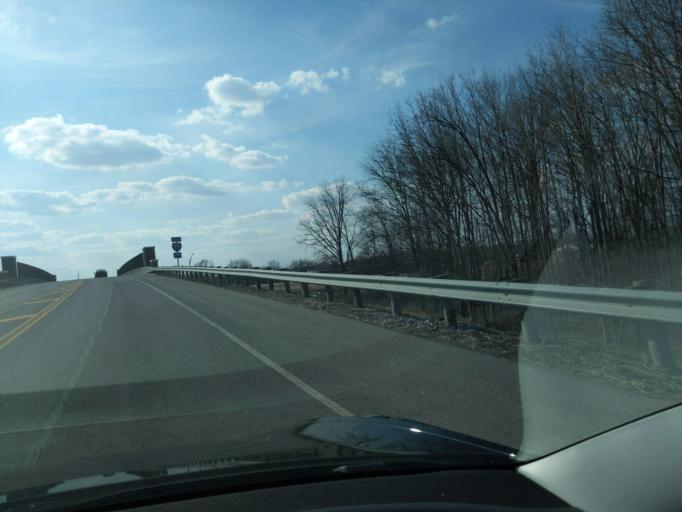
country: US
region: Ohio
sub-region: Allen County
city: Lima
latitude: 40.7171
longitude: -84.0738
